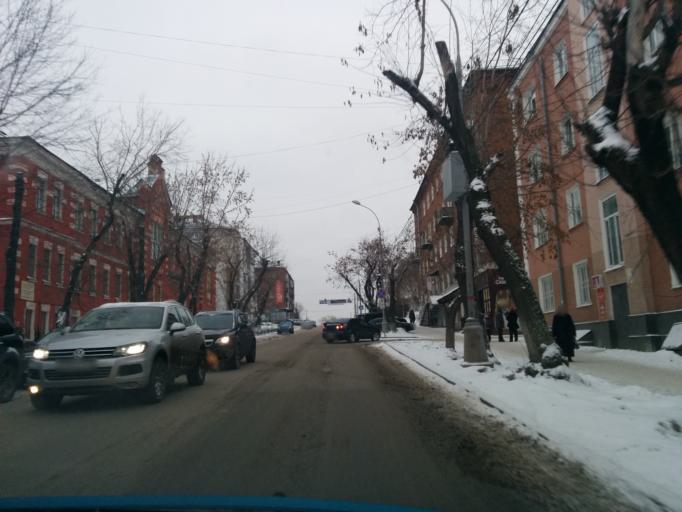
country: RU
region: Perm
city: Perm
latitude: 58.0052
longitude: 56.2062
